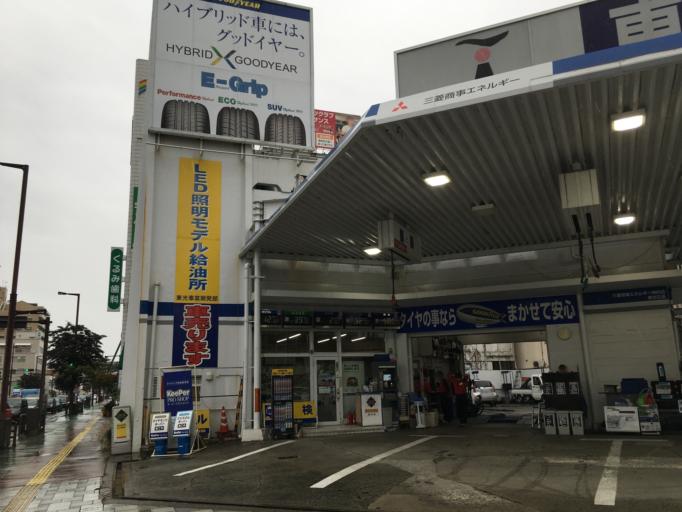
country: JP
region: Kumamoto
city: Kumamoto
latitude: 32.7948
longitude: 130.7254
